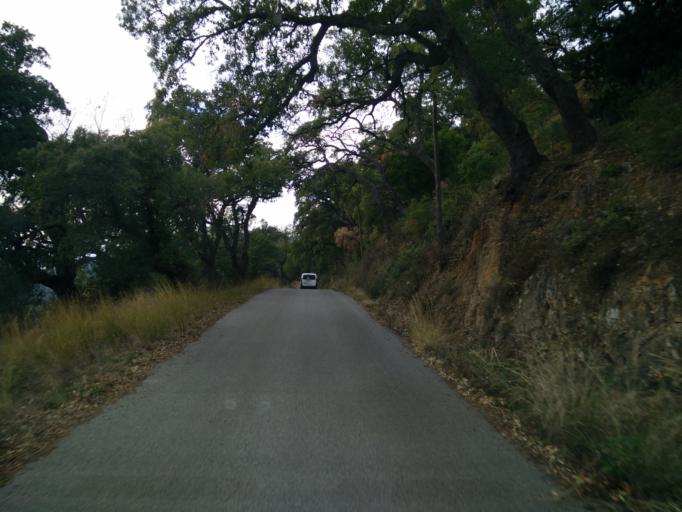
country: FR
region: Provence-Alpes-Cote d'Azur
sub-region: Departement du Var
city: Le Plan-de-la-Tour
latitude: 43.3670
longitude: 6.6043
